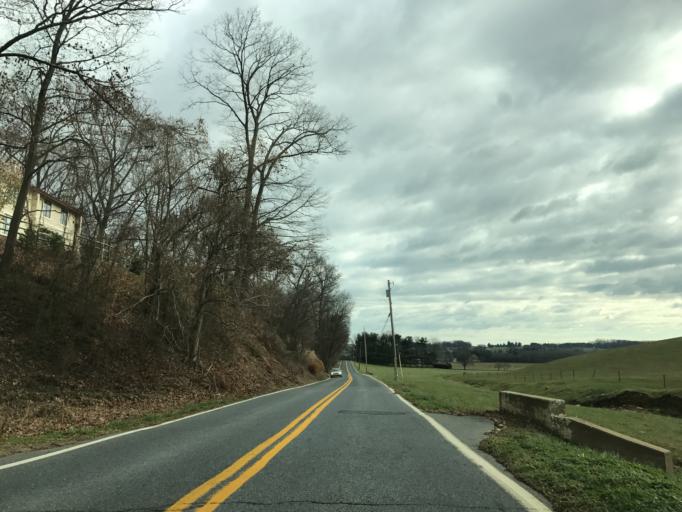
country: US
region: Maryland
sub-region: Baltimore County
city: Perry Hall
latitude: 39.4865
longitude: -76.5047
